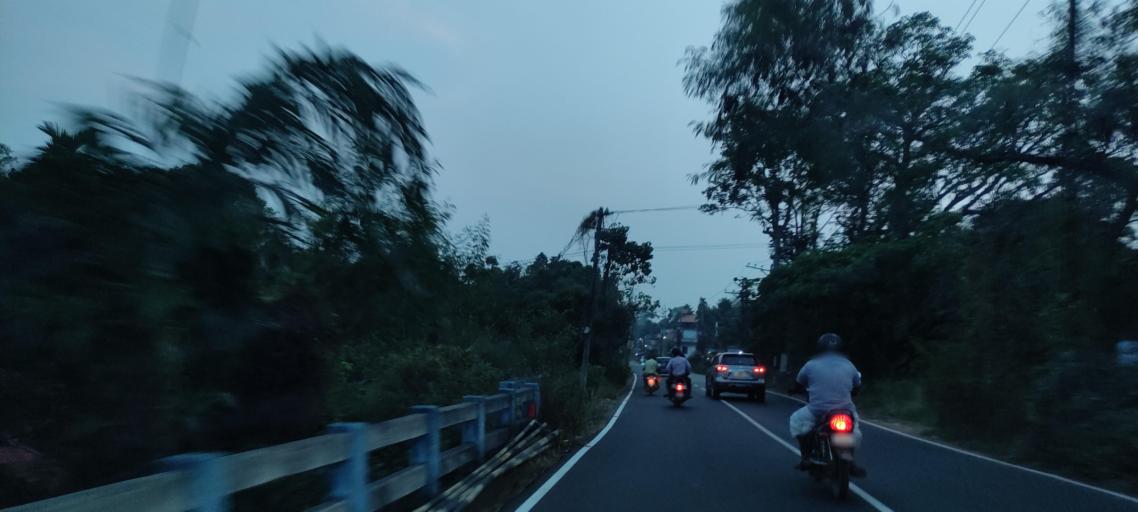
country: IN
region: Kerala
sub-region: Alappuzha
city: Mavelikara
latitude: 9.3256
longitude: 76.4615
